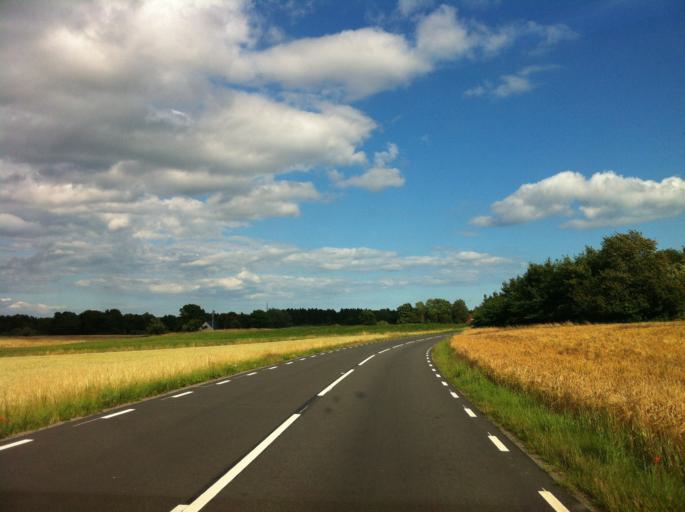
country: SE
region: Skane
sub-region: Ystads Kommun
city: Kopingebro
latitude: 55.3950
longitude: 14.1462
